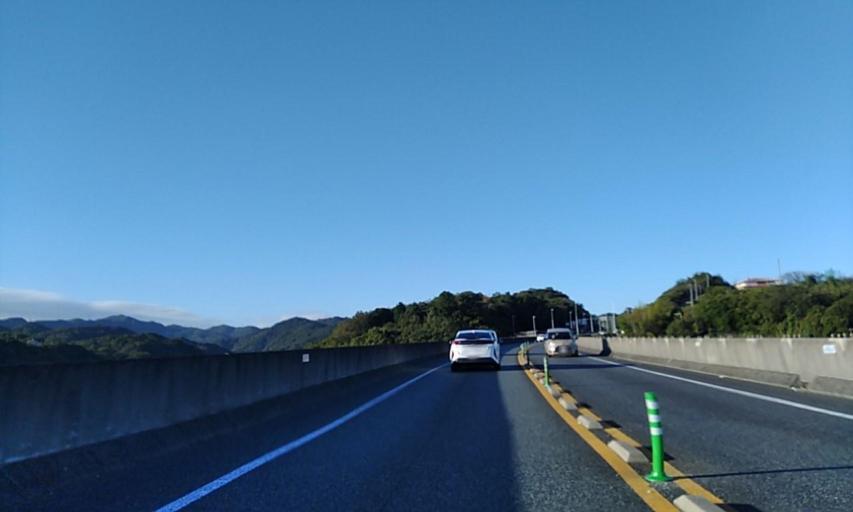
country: JP
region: Wakayama
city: Iwade
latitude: 34.3404
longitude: 135.2481
